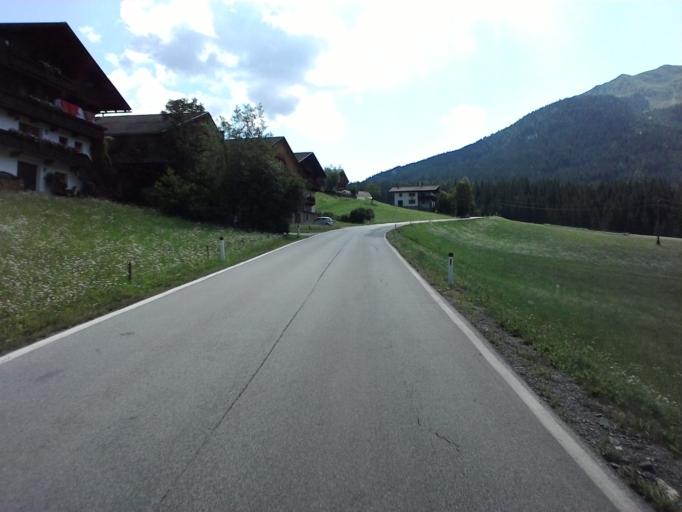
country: AT
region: Tyrol
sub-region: Politischer Bezirk Lienz
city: Kartitsch
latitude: 46.7212
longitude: 12.5191
